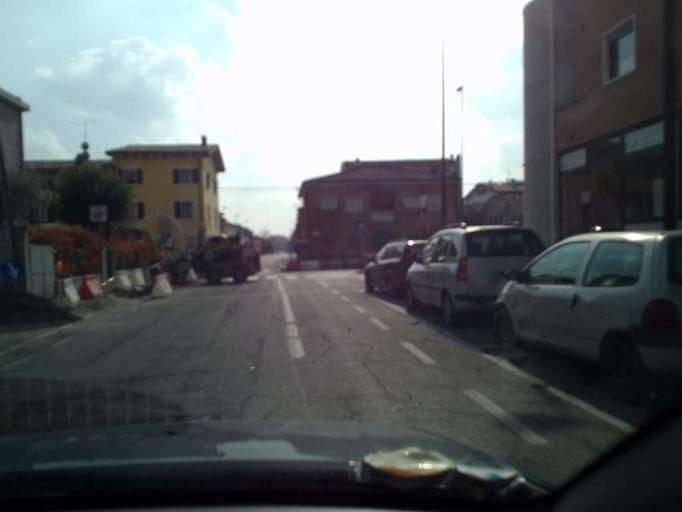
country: IT
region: Veneto
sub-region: Provincia di Verona
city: Villafranca di Verona
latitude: 45.3544
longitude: 10.8400
